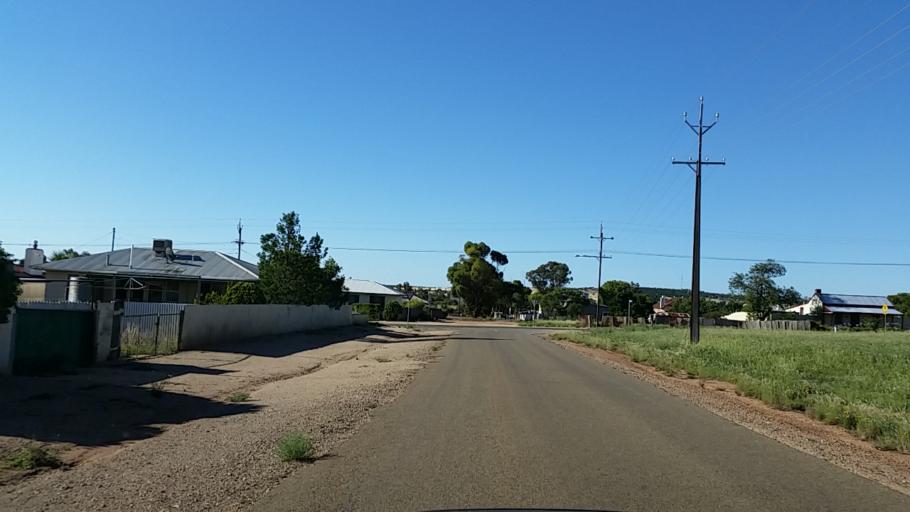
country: AU
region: South Australia
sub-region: Peterborough
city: Peterborough
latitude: -32.9805
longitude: 138.8282
